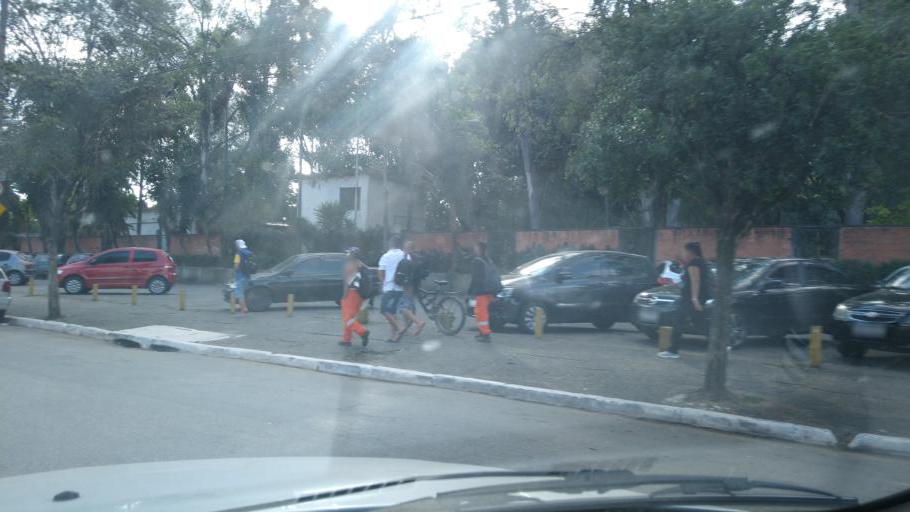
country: BR
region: Sao Paulo
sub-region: Sao Paulo
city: Sao Paulo
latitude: -23.5254
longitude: -46.6221
